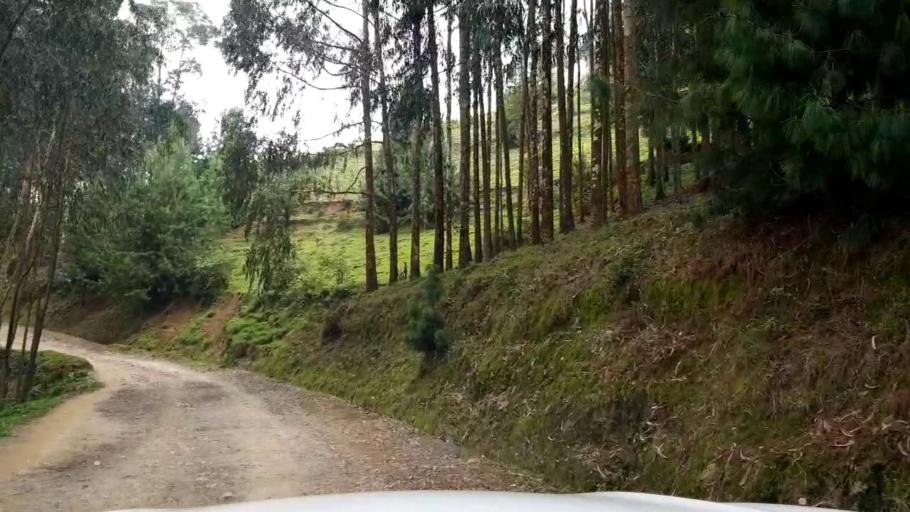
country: RW
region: Western Province
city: Kibuye
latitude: -1.9567
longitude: 29.4752
